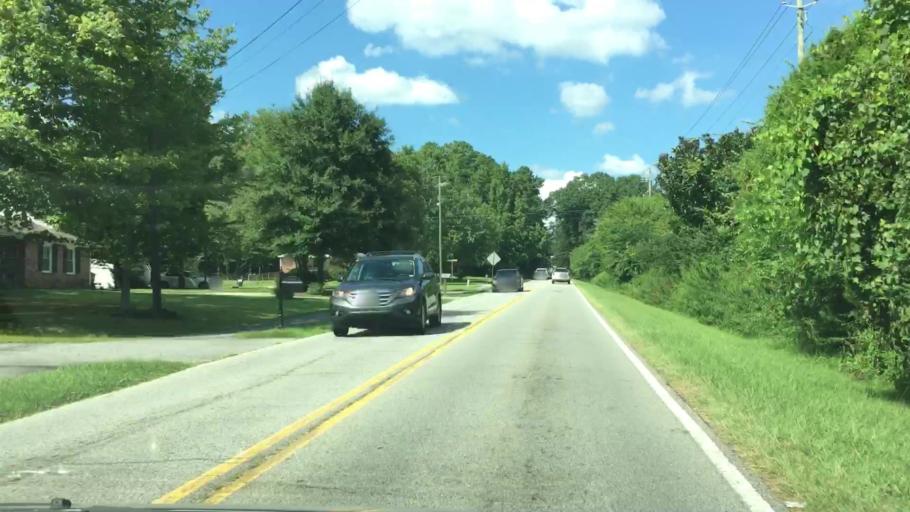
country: US
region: Georgia
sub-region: Fayette County
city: Fayetteville
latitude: 33.4383
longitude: -84.4590
